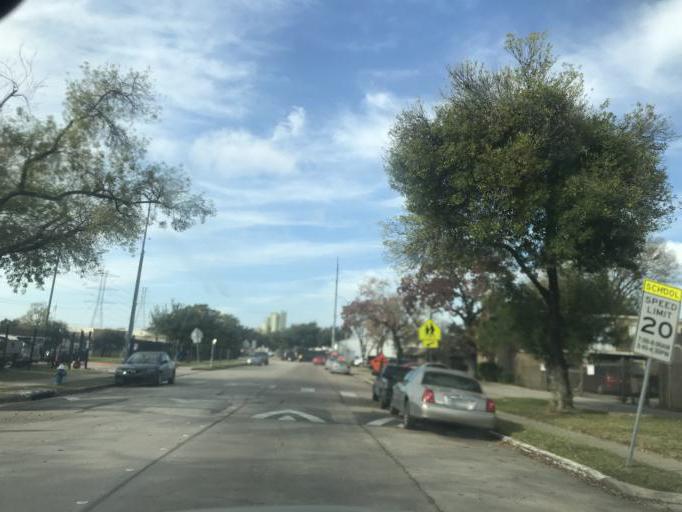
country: US
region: Texas
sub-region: Harris County
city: Bellaire
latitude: 29.7227
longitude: -95.4794
